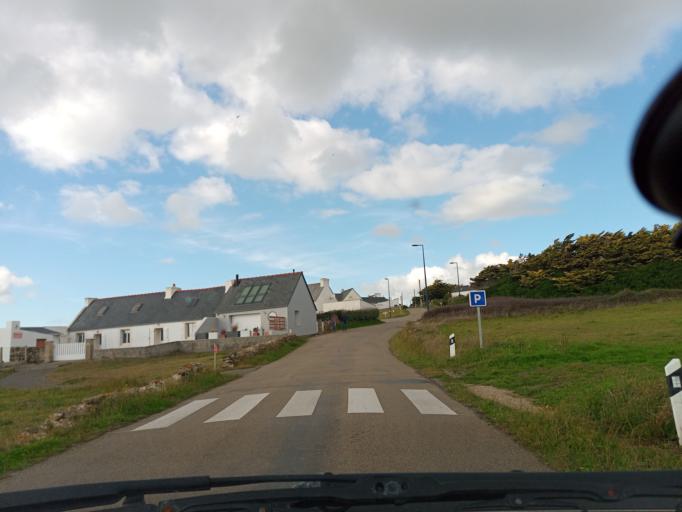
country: FR
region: Brittany
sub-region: Departement du Finistere
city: Plozevet
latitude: 47.9804
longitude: -4.4494
